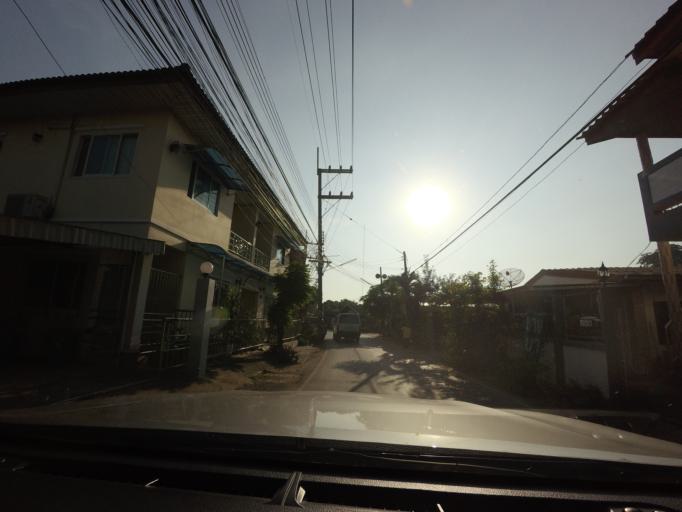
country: TH
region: Lampang
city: Lampang
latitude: 18.2618
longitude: 99.4574
